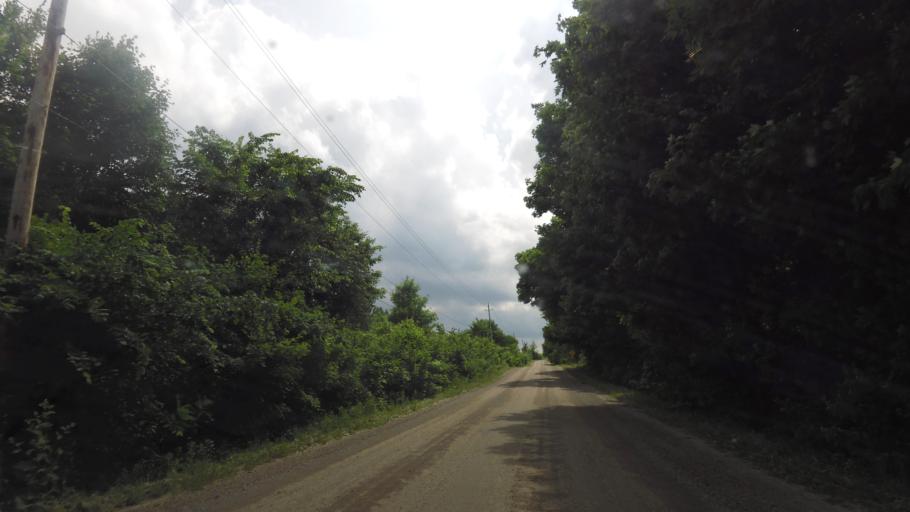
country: CA
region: Ontario
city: Orangeville
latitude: 43.8765
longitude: -79.9286
